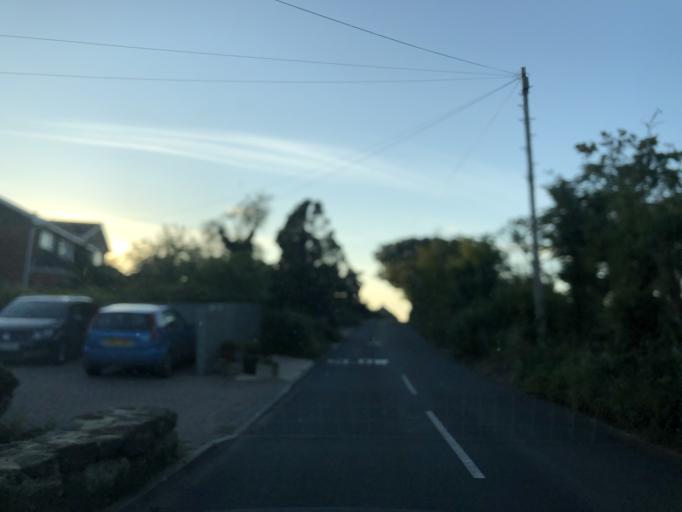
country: GB
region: England
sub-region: Isle of Wight
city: Newport
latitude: 50.6503
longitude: -1.2815
